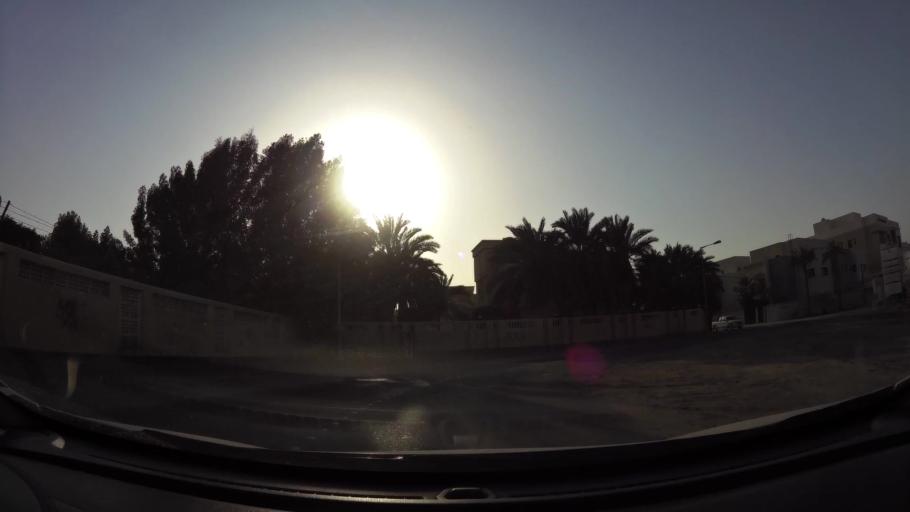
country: BH
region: Manama
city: Jidd Hafs
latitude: 26.2032
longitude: 50.4899
